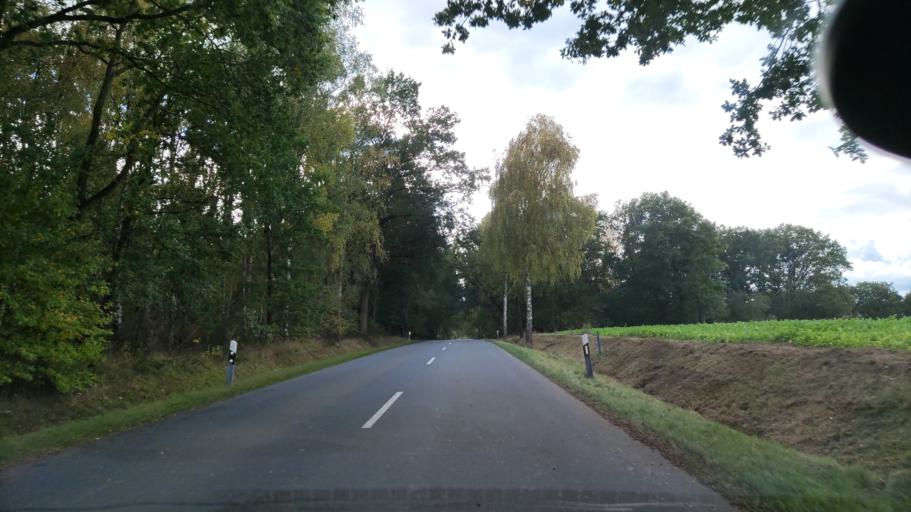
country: DE
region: Lower Saxony
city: Romstedt
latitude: 53.0870
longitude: 10.6438
